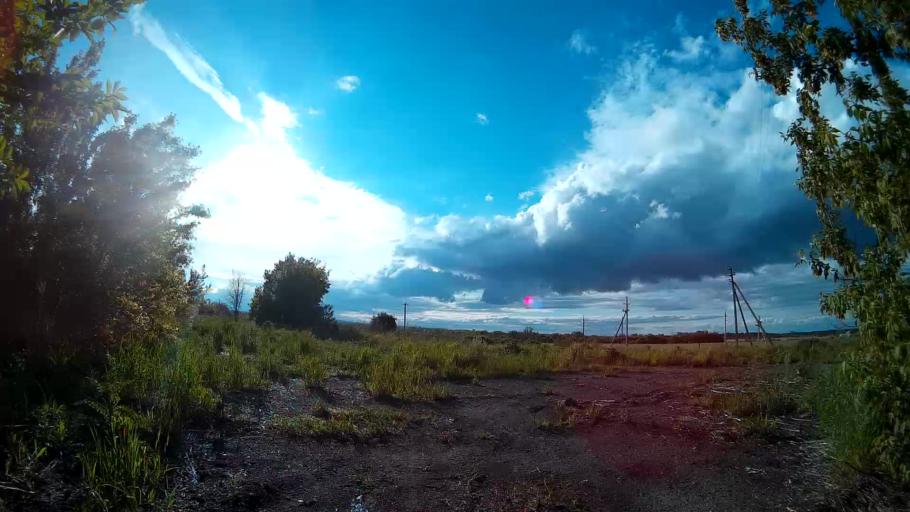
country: RU
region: Ulyanovsk
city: Novoul'yanovsk
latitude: 54.2070
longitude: 48.2712
